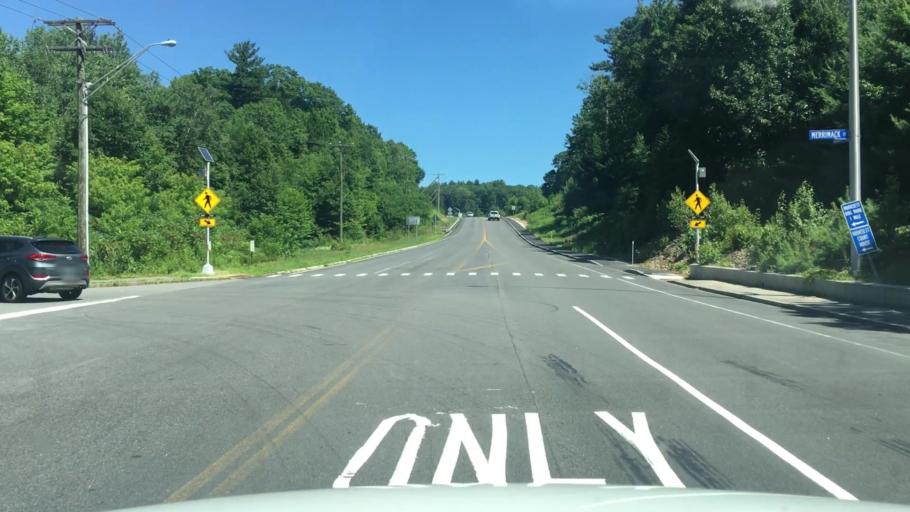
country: US
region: New Hampshire
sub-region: Merrimack County
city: Hooksett
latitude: 43.0937
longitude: -71.4617
